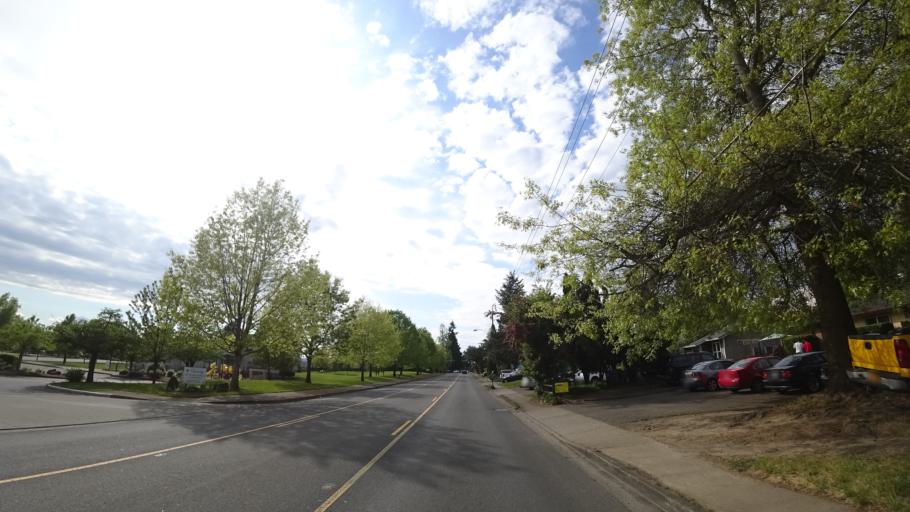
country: US
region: Oregon
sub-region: Washington County
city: Hillsboro
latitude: 45.5035
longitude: -122.9606
